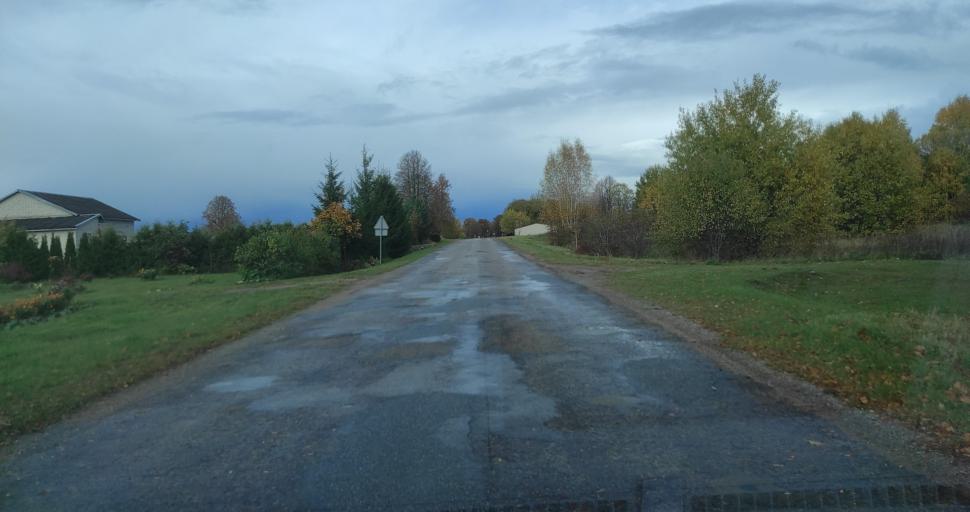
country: LV
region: Vainode
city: Vainode
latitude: 56.5674
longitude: 21.9044
